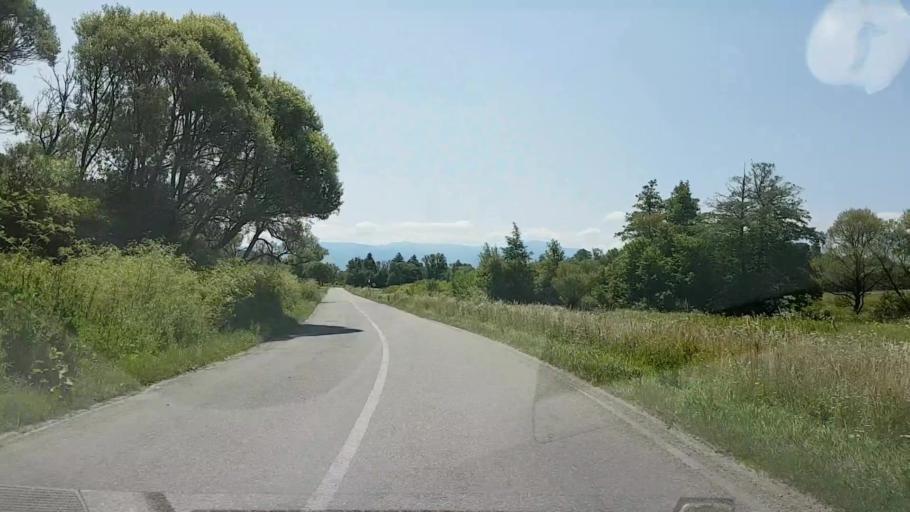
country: RO
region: Brasov
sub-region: Comuna Voila
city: Voila
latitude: 45.8616
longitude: 24.8255
